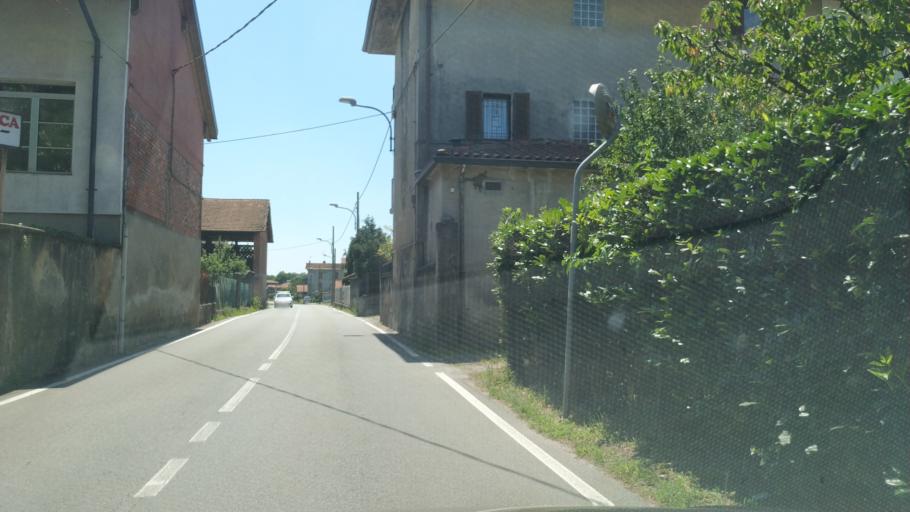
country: IT
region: Piedmont
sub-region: Provincia di Novara
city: Cureggio
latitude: 45.6876
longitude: 8.4576
